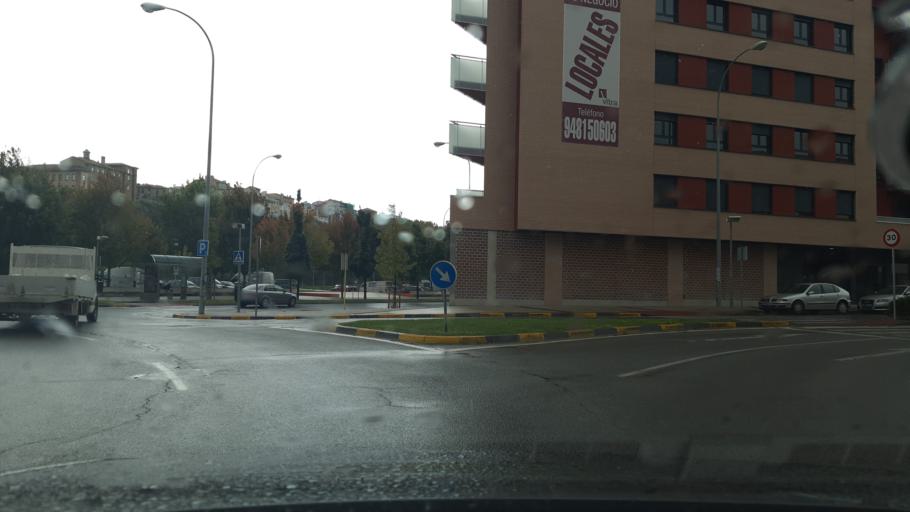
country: ES
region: Navarre
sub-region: Provincia de Navarra
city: Pamplona
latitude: 42.8228
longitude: -1.6458
